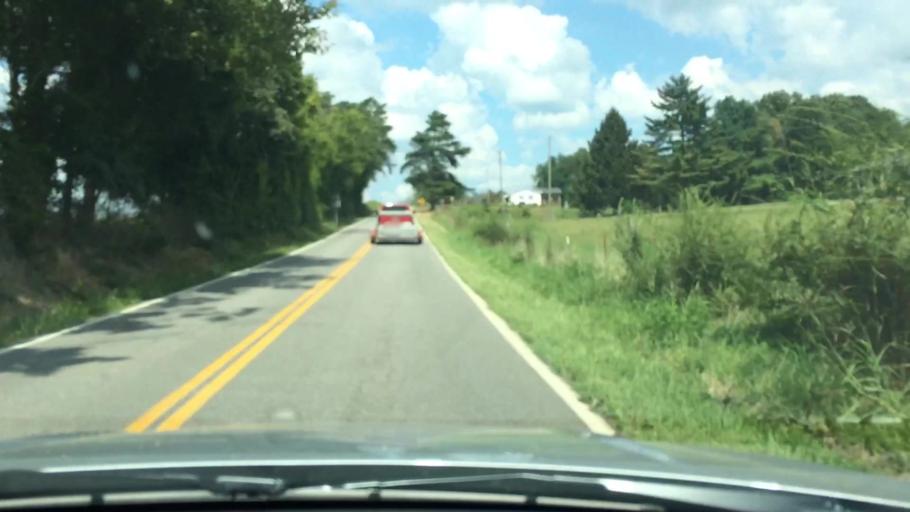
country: US
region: Tennessee
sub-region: Monroe County
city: Sweetwater
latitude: 35.5274
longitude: -84.4611
